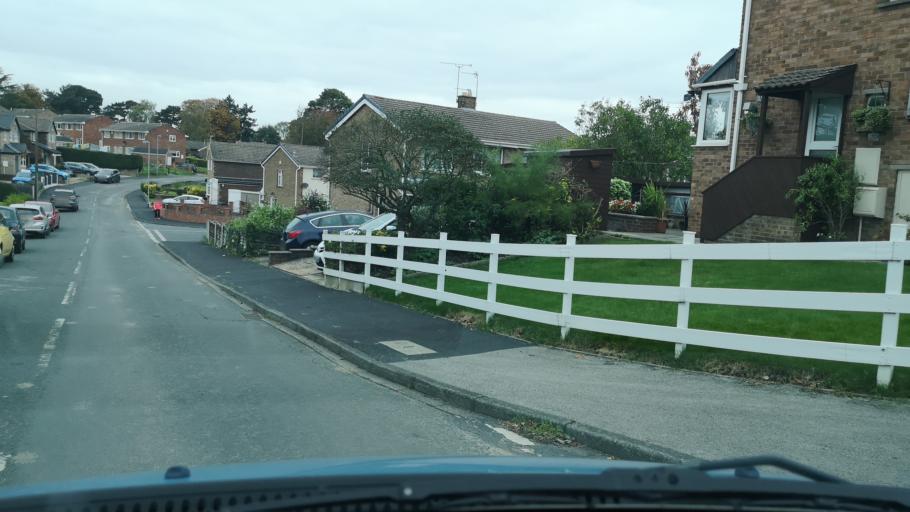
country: GB
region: England
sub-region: City and Borough of Wakefield
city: Low Ackworth
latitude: 53.6432
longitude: -1.3409
